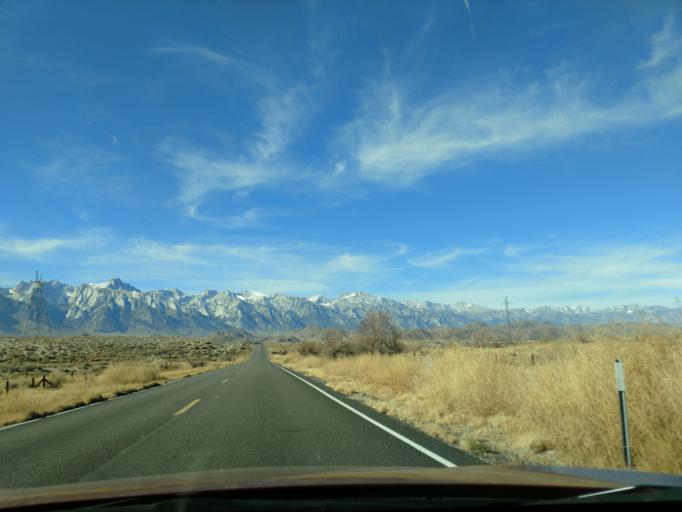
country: US
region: California
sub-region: Inyo County
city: Lone Pine
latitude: 36.5748
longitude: -118.0135
